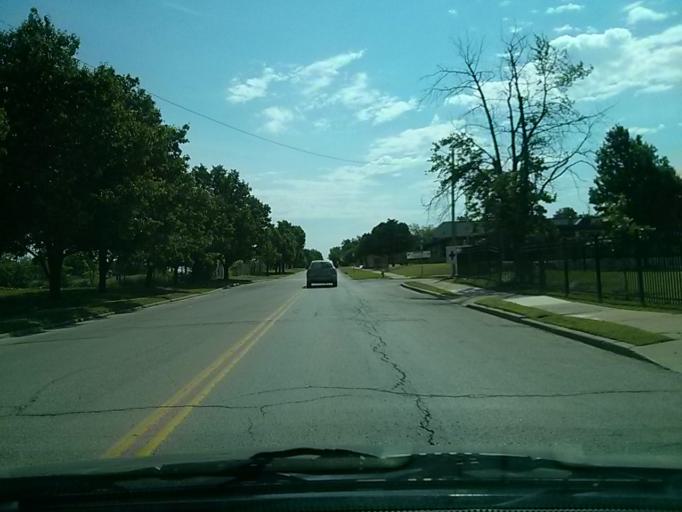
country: US
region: Oklahoma
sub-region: Tulsa County
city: Tulsa
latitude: 36.1598
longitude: -95.9566
